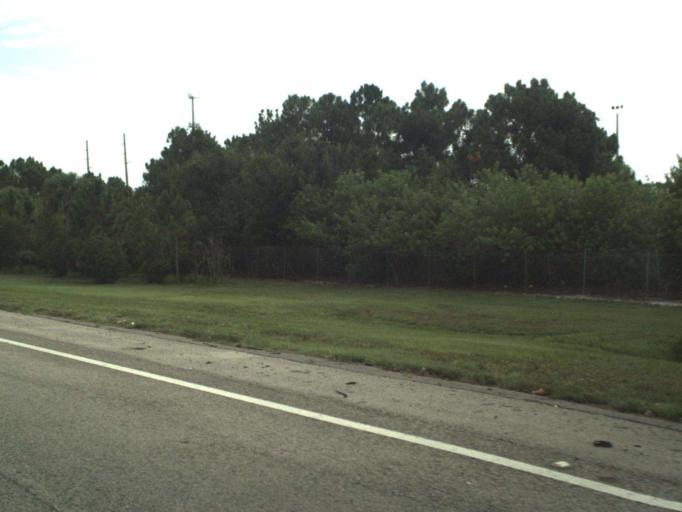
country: US
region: Florida
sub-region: Saint Lucie County
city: River Park
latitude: 27.3184
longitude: -80.4134
